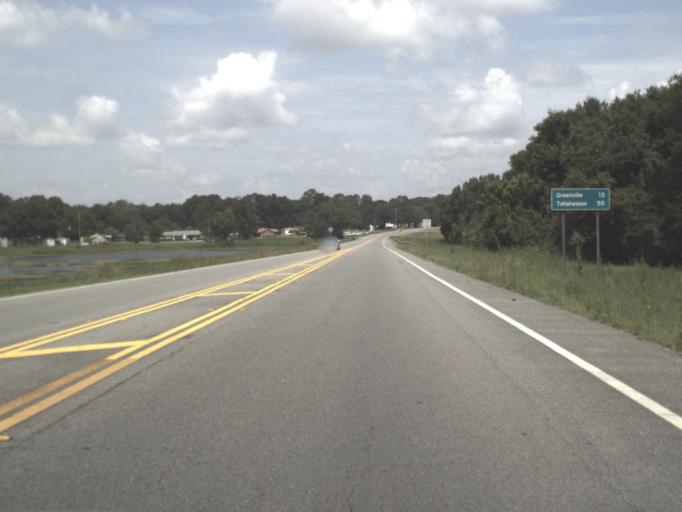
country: US
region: Florida
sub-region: Madison County
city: Madison
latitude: 30.4730
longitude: -83.4290
